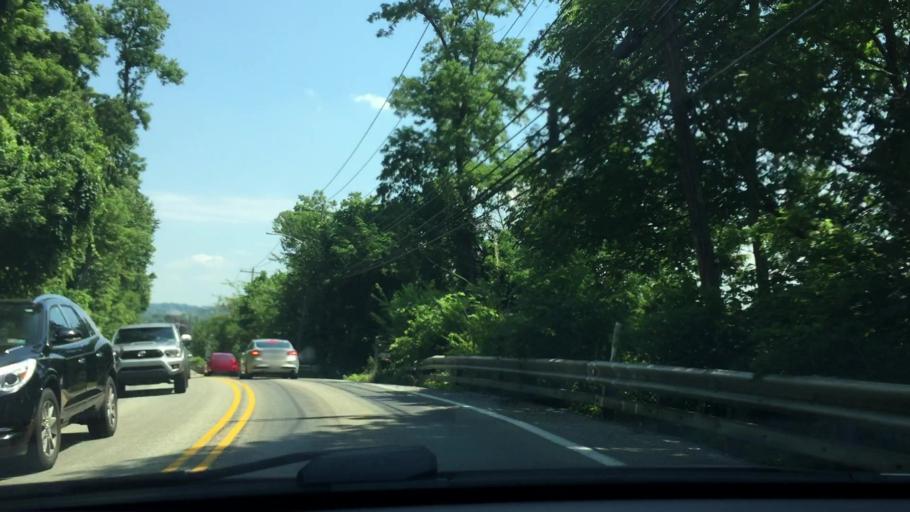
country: US
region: Pennsylvania
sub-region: Allegheny County
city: Bridgeville
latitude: 40.3390
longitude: -80.1238
